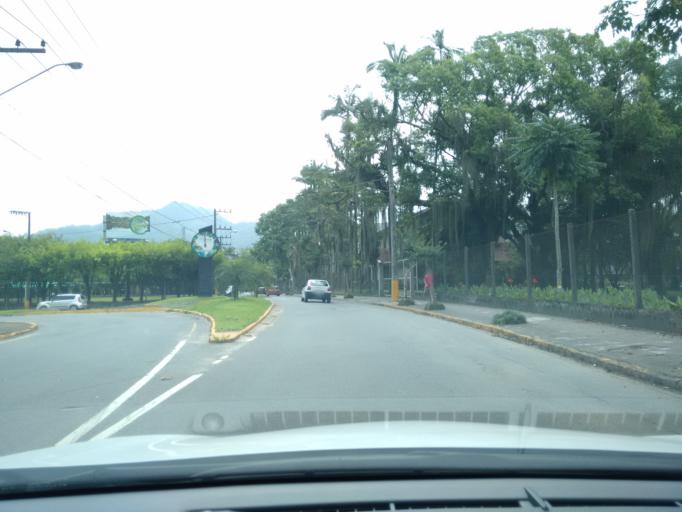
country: BR
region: Santa Catarina
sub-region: Jaragua Do Sul
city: Jaragua do Sul
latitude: -26.5136
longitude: -49.1241
